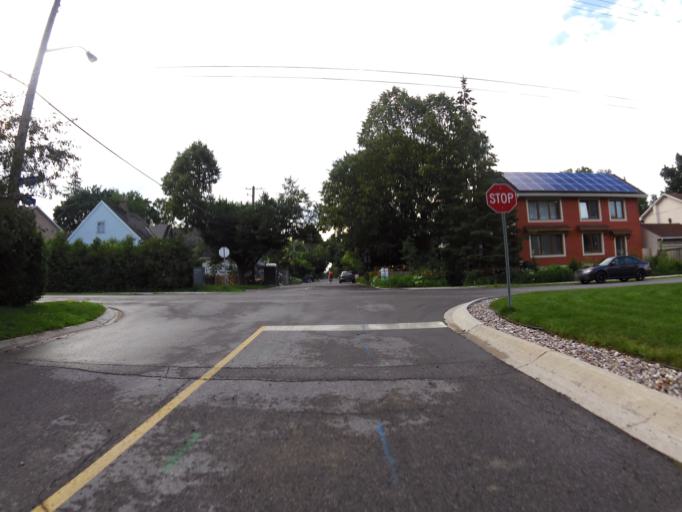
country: CA
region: Ontario
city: Ottawa
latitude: 45.3858
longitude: -75.7549
